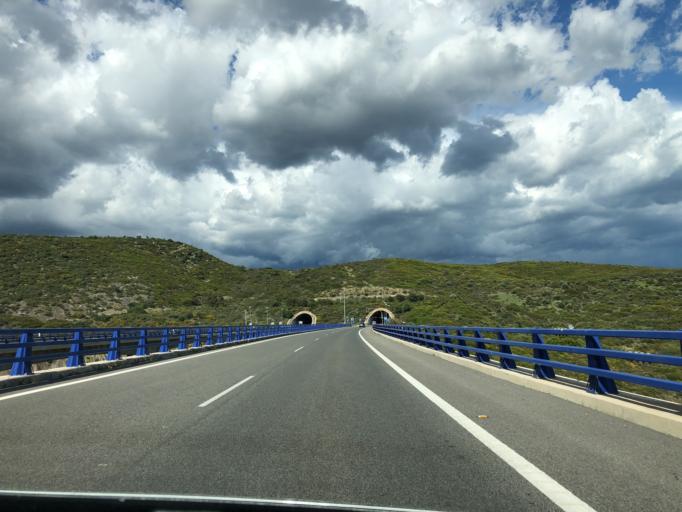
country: ES
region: Andalusia
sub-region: Provincia de Malaga
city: Manilva
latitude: 36.4223
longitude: -5.2161
